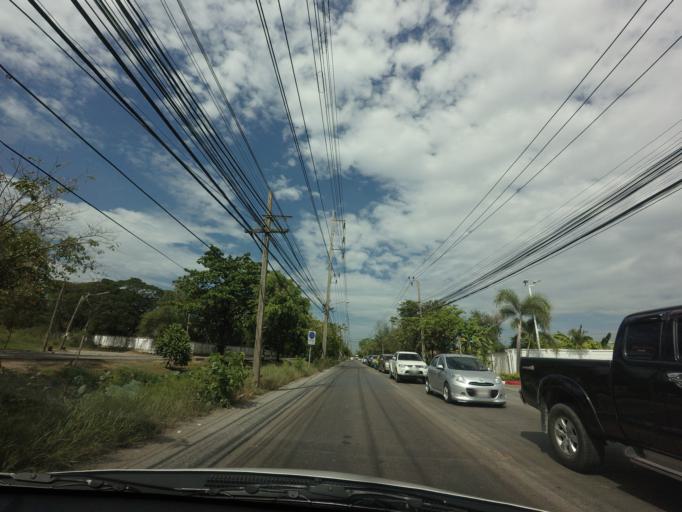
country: TH
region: Bangkok
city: Phra Khanong
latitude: 13.6671
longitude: 100.5918
